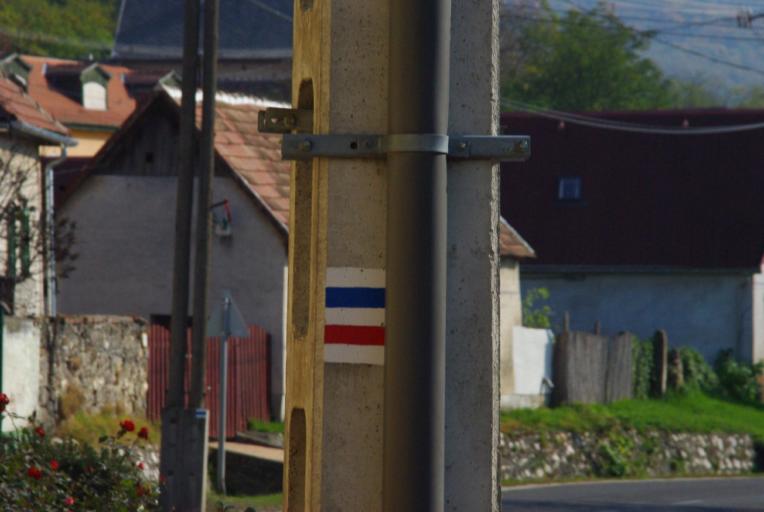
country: HU
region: Komarom-Esztergom
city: Piliscsev
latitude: 47.6786
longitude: 18.8193
